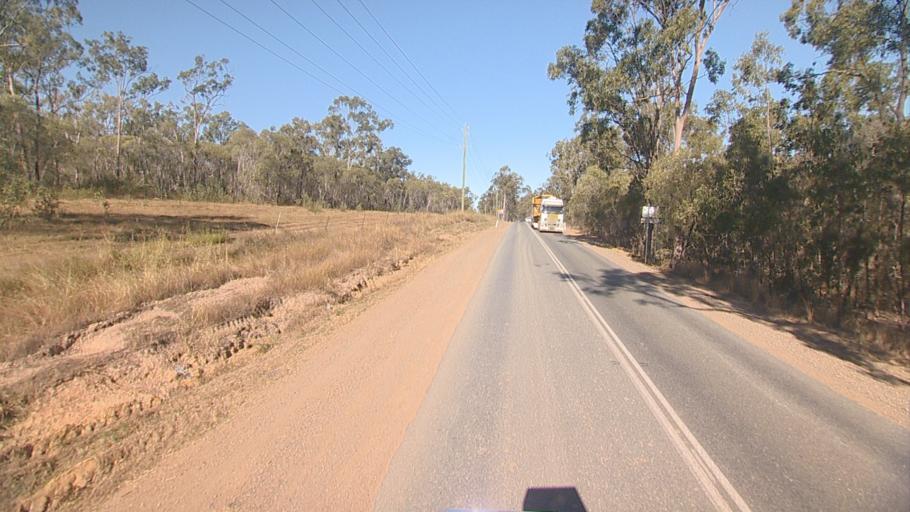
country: AU
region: Queensland
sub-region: Logan
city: North Maclean
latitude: -27.7456
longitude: 152.9896
